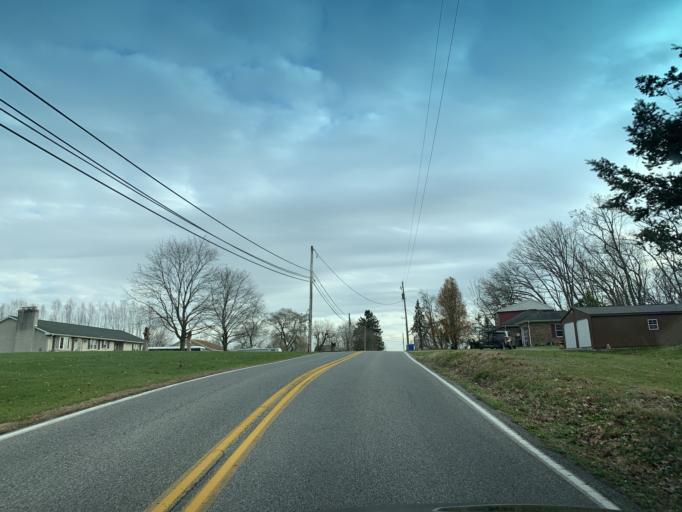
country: US
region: Pennsylvania
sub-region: York County
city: Manchester
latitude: 40.0865
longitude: -76.7540
